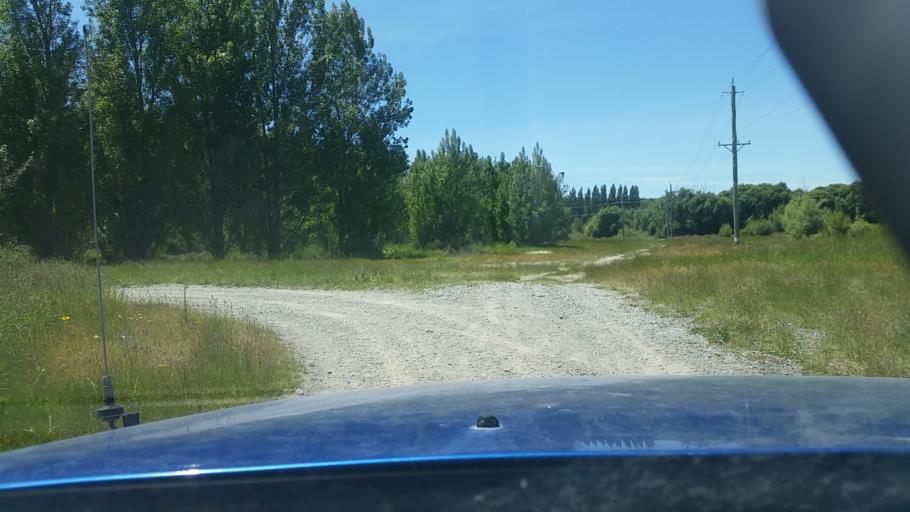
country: NZ
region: Canterbury
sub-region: Ashburton District
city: Tinwald
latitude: -43.9454
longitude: 171.7739
